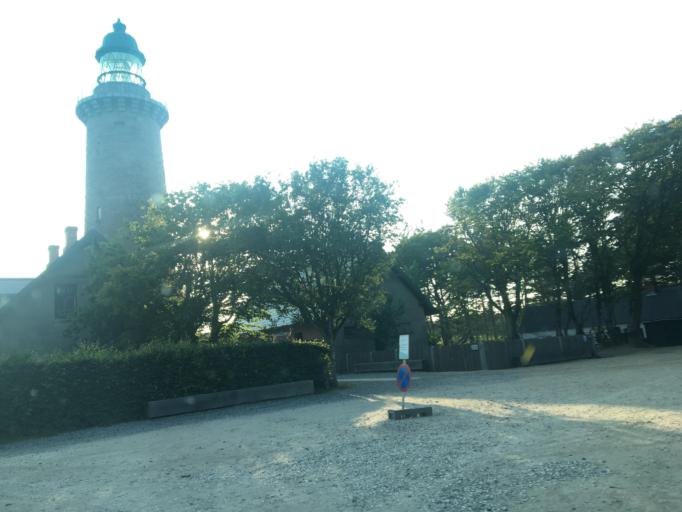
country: DK
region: Central Jutland
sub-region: Lemvig Kommune
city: Thyboron
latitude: 56.8234
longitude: 8.2636
